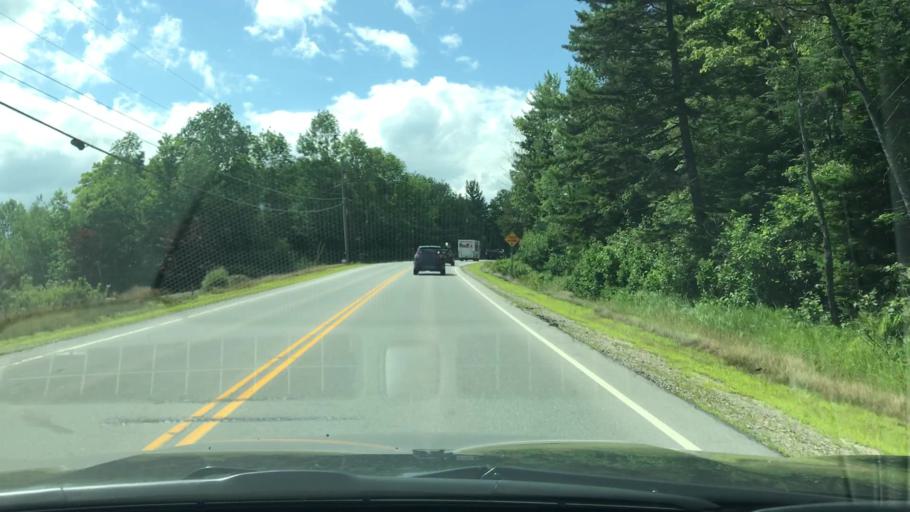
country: US
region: New Hampshire
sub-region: Coos County
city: Jefferson
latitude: 44.3631
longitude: -71.3883
